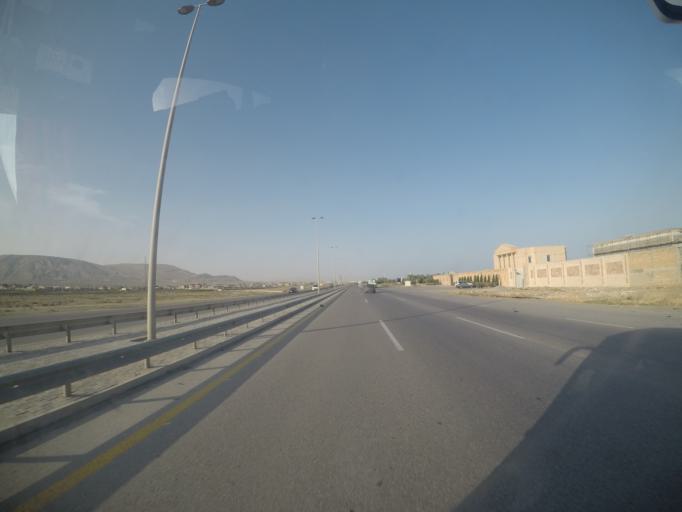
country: AZ
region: Baki
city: Qobustan
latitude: 40.1962
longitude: 49.5108
